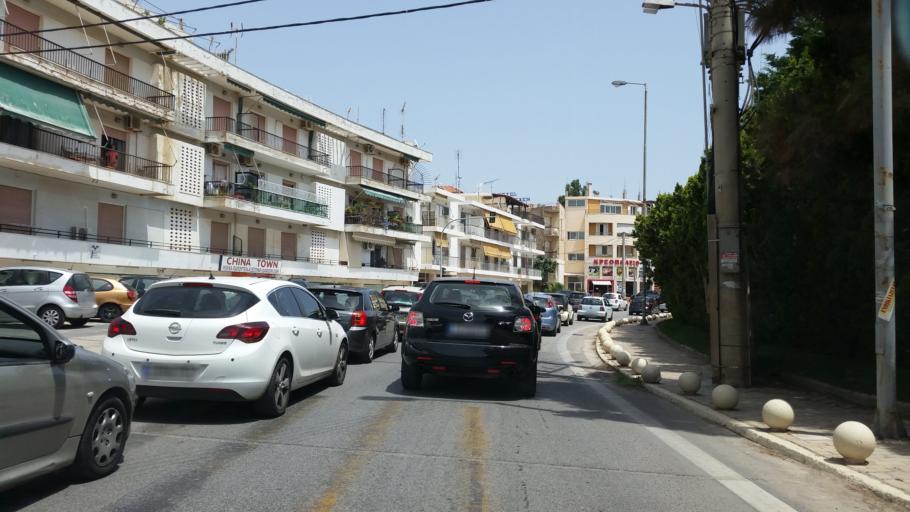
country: GR
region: Attica
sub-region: Nomarchia Anatolikis Attikis
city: Palaia Fokaia
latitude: 37.7244
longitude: 23.9446
